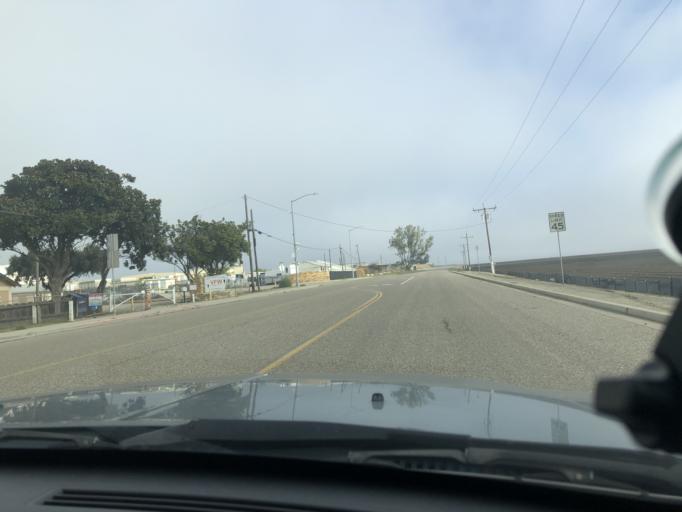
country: US
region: California
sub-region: Monterey County
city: King City
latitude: 36.2213
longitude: -121.1186
